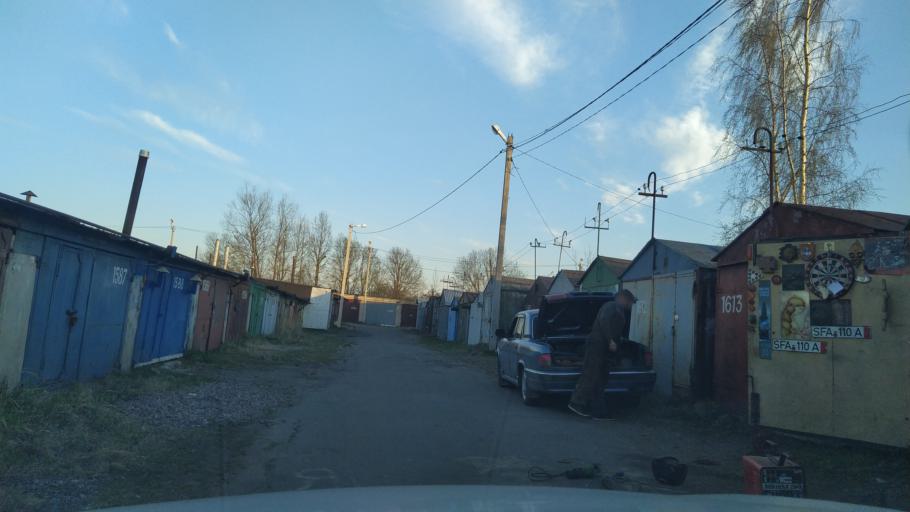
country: RU
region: St.-Petersburg
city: Pushkin
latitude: 59.6918
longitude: 30.3942
